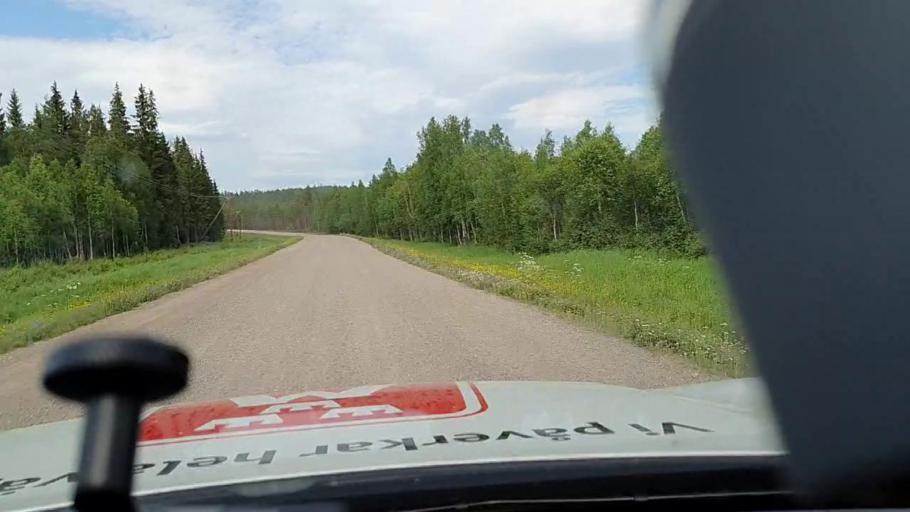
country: SE
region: Norrbotten
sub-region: Alvsbyns Kommun
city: AElvsbyn
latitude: 66.1203
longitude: 20.9866
